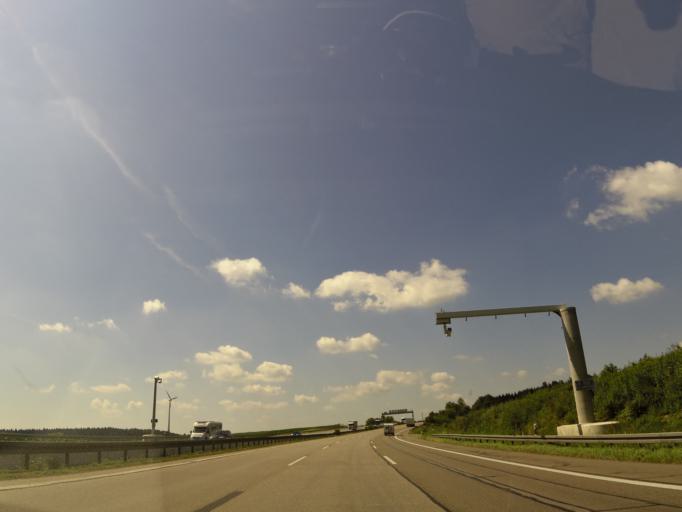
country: DE
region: Bavaria
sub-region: Upper Bavaria
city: Schweitenkirchen
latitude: 48.5342
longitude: 11.5947
